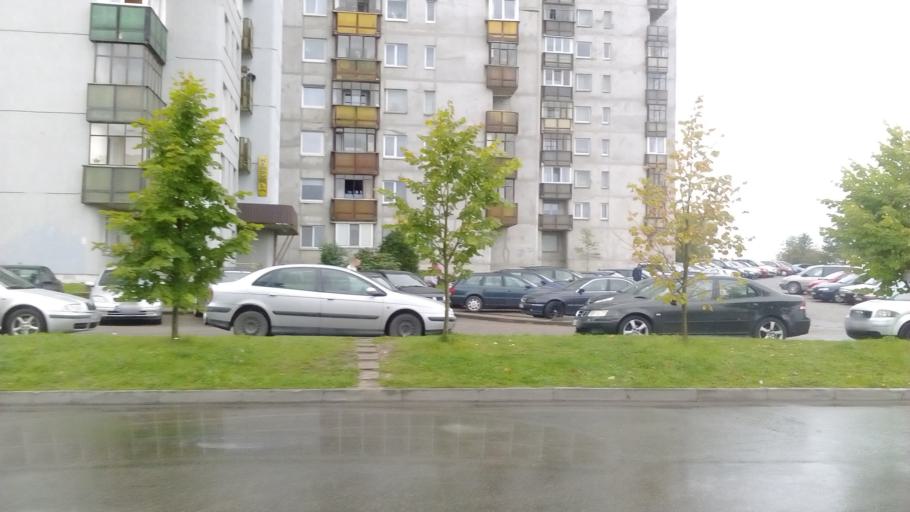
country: LT
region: Alytaus apskritis
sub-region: Alytus
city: Alytus
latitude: 54.3933
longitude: 24.0173
